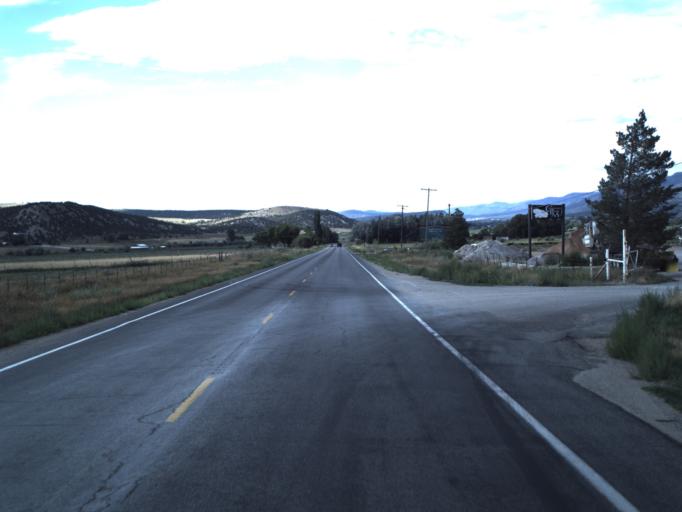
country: US
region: Utah
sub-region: Sanpete County
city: Mount Pleasant
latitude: 39.5739
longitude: -111.4554
